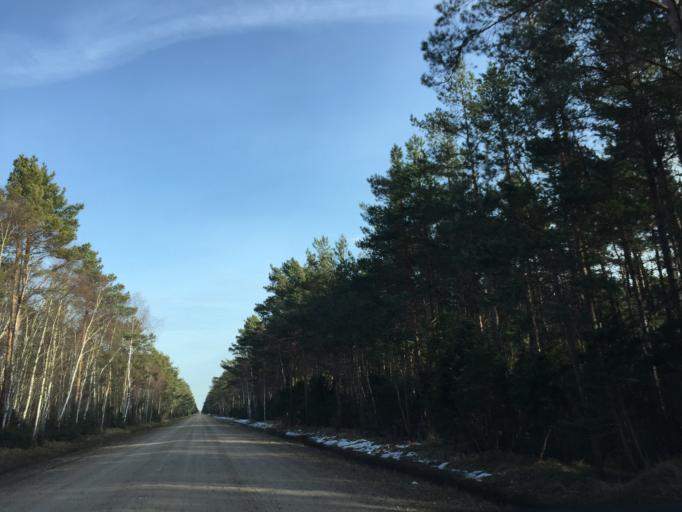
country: EE
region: Saare
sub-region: Kuressaare linn
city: Kuressaare
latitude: 58.2928
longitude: 21.9417
